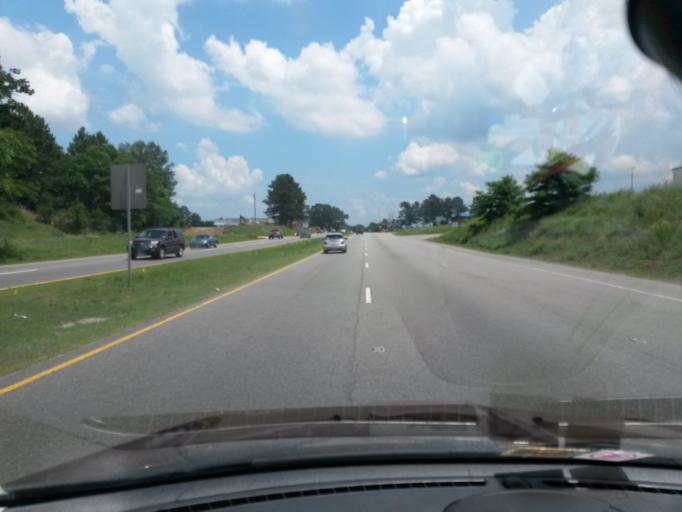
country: US
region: Virginia
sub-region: Chesterfield County
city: Chester
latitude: 37.3518
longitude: -77.3900
